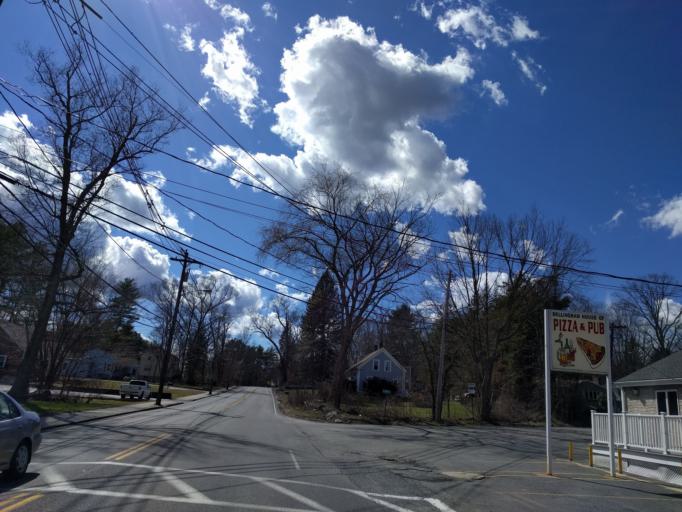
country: US
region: Massachusetts
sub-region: Norfolk County
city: Medway
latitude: 42.1333
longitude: -71.4471
